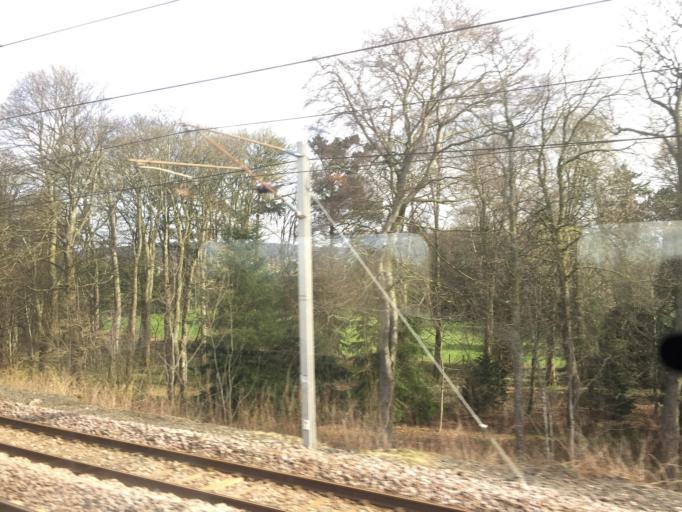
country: GB
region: England
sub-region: Cumbria
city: Penrith
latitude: 54.6501
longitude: -2.7667
